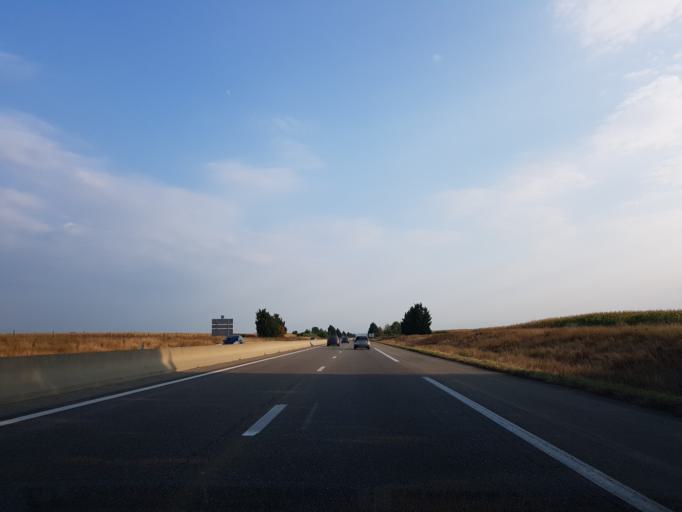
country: FR
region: Alsace
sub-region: Departement du Haut-Rhin
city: Battenheim
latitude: 47.8316
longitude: 7.3941
